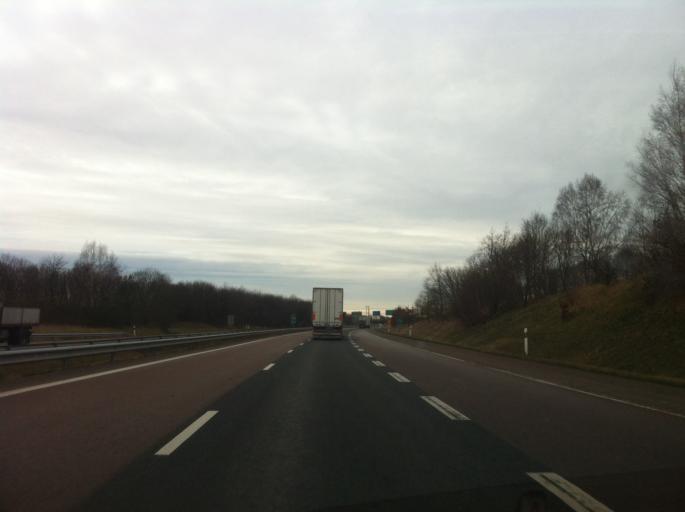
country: SE
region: Skane
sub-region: Astorps Kommun
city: Astorp
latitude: 56.1415
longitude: 12.9542
